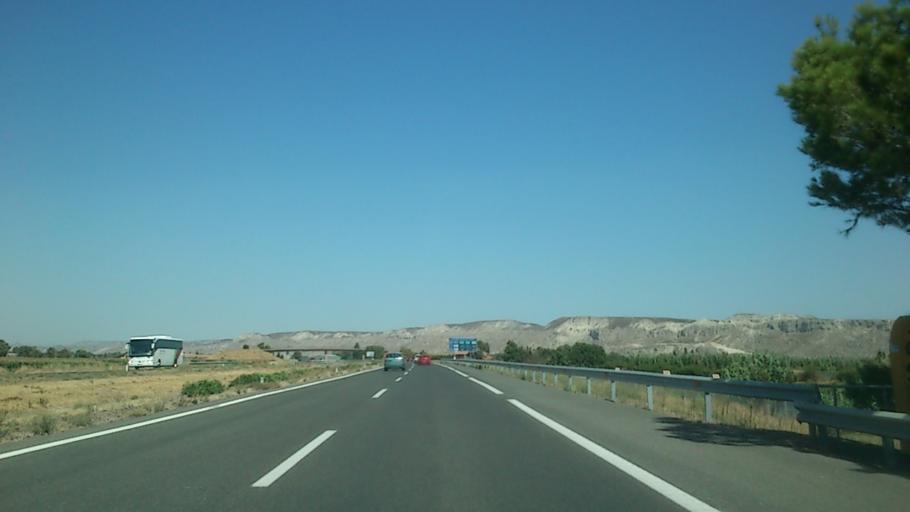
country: ES
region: Aragon
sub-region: Provincia de Zaragoza
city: Utebo
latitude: 41.7075
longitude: -0.9810
